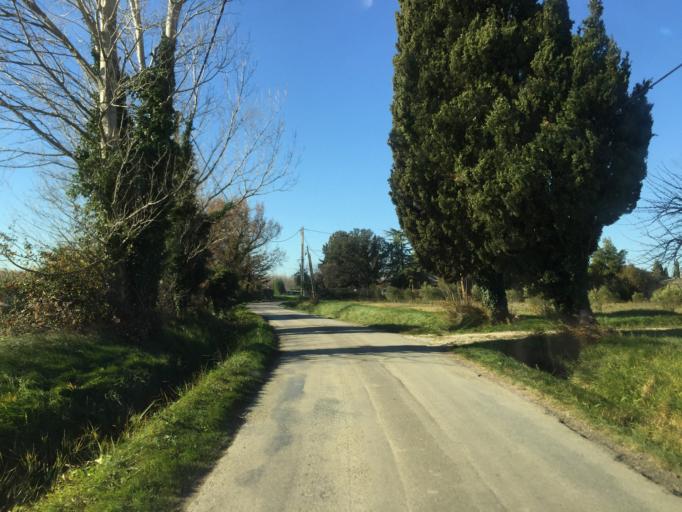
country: FR
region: Provence-Alpes-Cote d'Azur
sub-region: Departement du Vaucluse
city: Courthezon
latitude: 44.0821
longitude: 4.8940
